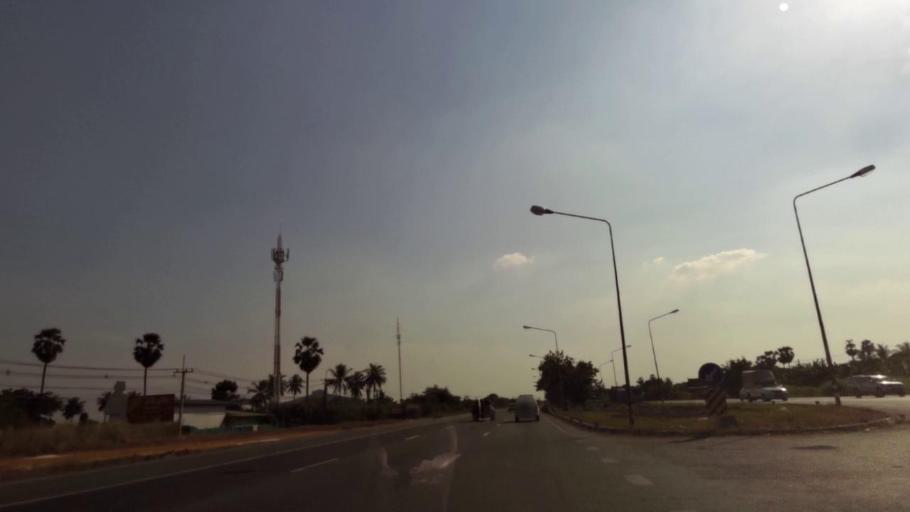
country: TH
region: Ang Thong
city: Chaiyo
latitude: 14.6394
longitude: 100.4745
